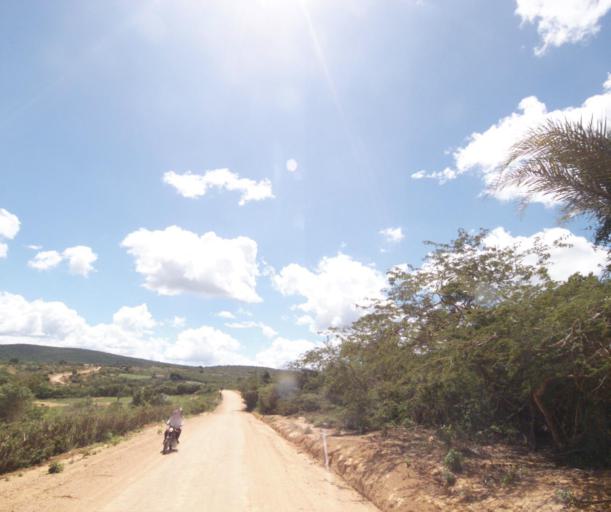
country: BR
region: Bahia
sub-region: Pocoes
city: Pocoes
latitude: -14.2998
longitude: -40.6551
